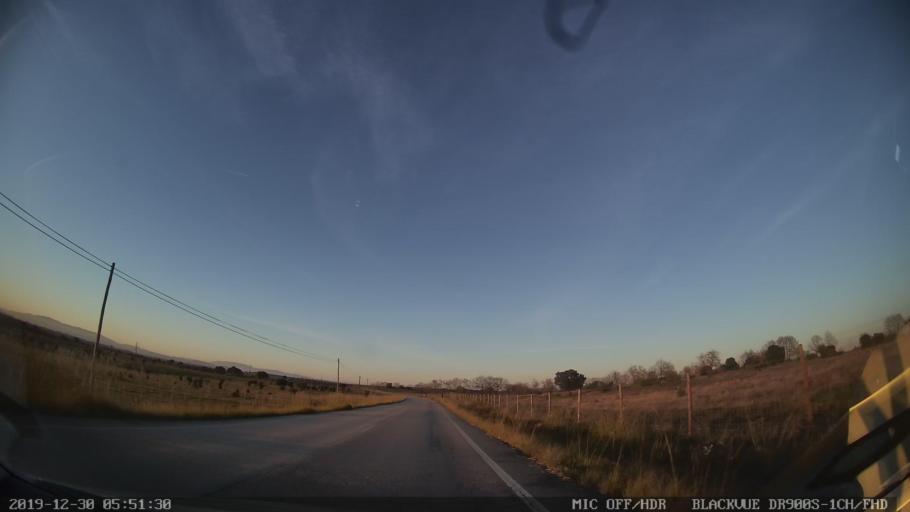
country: PT
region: Castelo Branco
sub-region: Idanha-A-Nova
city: Idanha-a-Nova
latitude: 39.9954
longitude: -7.2443
